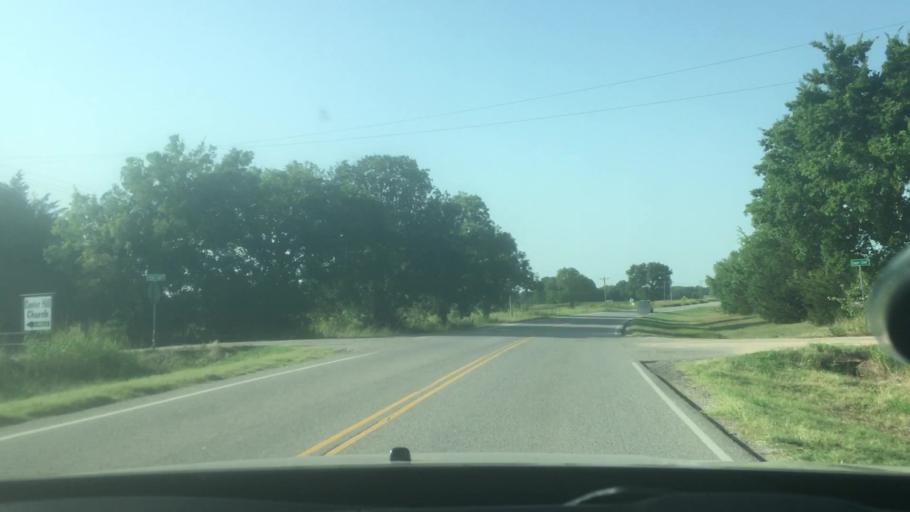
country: US
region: Oklahoma
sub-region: Bryan County
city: Durant
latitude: 34.1866
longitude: -96.4165
